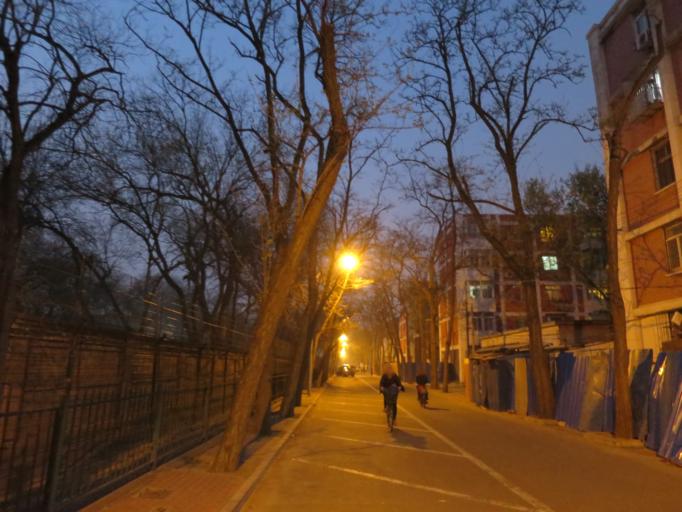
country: CN
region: Beijing
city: Chaowai
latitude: 39.9093
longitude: 116.4431
